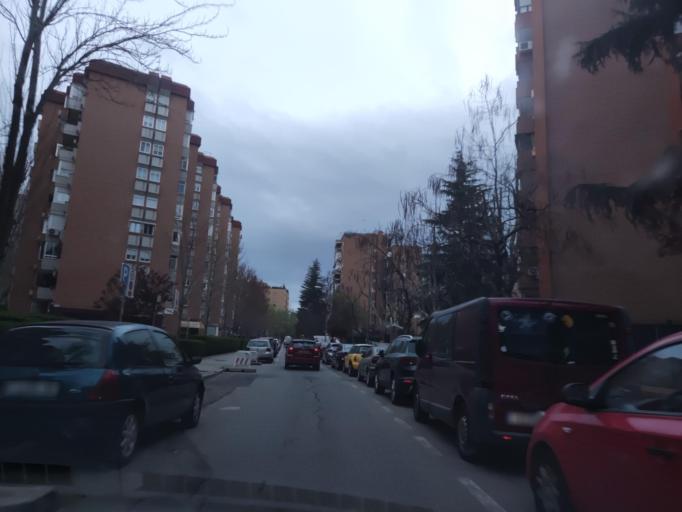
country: ES
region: Madrid
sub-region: Provincia de Madrid
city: Hortaleza
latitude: 40.4677
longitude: -3.6351
